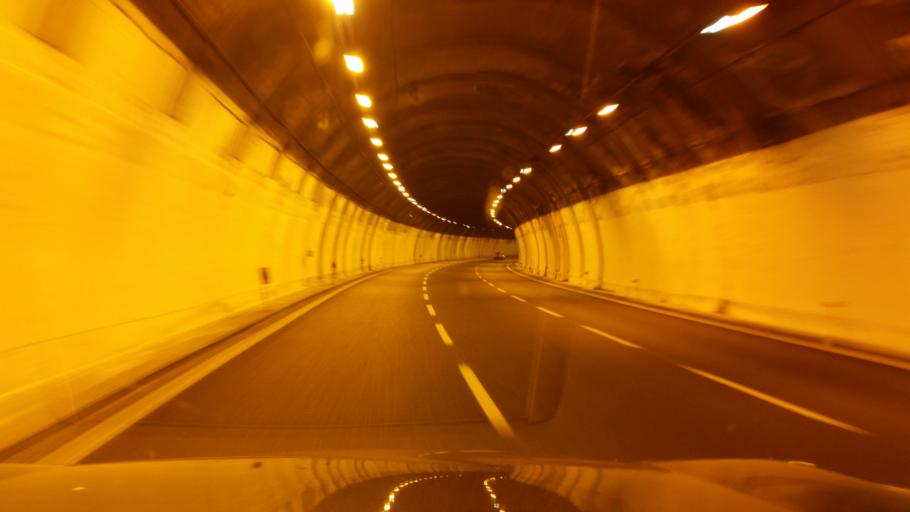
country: IT
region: Liguria
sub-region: Provincia di Genova
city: Mele
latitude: 44.4281
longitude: 8.7399
